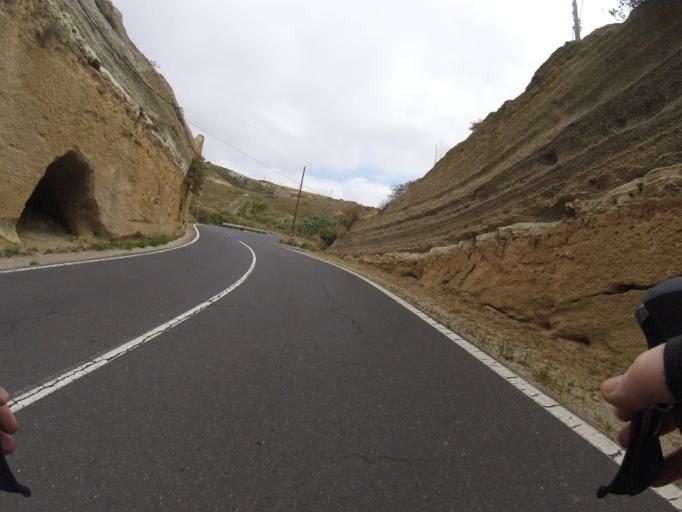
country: ES
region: Canary Islands
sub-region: Provincia de Santa Cruz de Tenerife
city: Guimar
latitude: 28.2768
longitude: -16.4122
